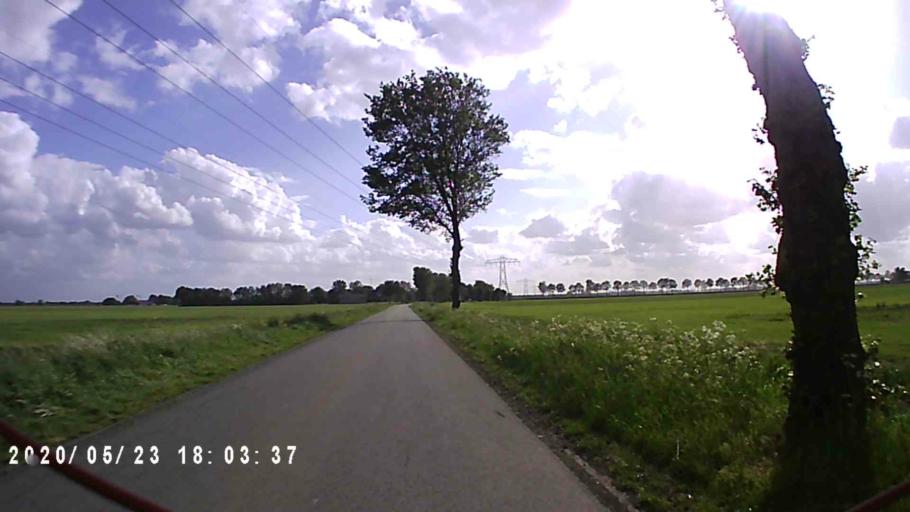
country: NL
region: Groningen
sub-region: Gemeente Slochteren
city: Slochteren
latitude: 53.2448
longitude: 6.7247
